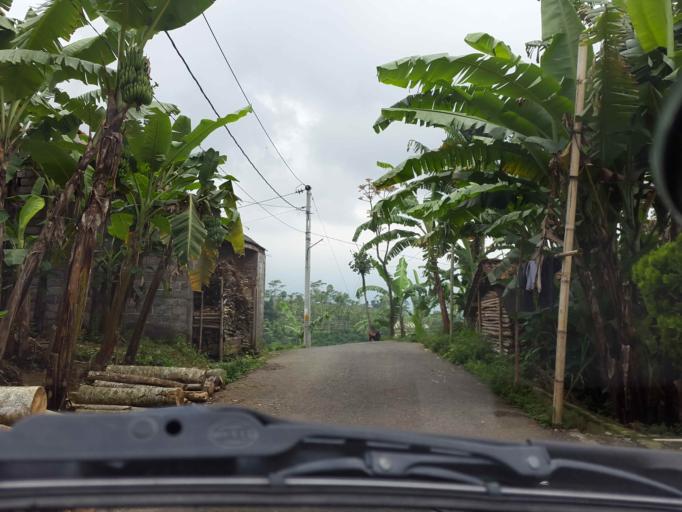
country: ID
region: Central Java
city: Wonosobo
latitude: -7.2879
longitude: 109.8781
